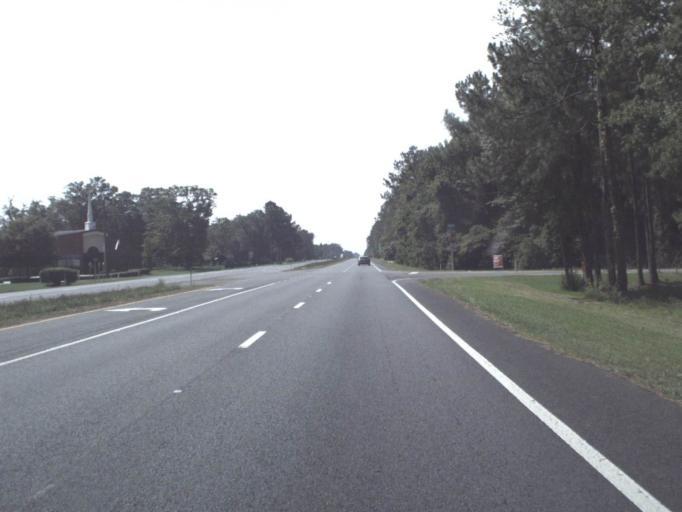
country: US
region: Florida
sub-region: Nassau County
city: Hilliard
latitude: 30.7305
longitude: -81.9454
